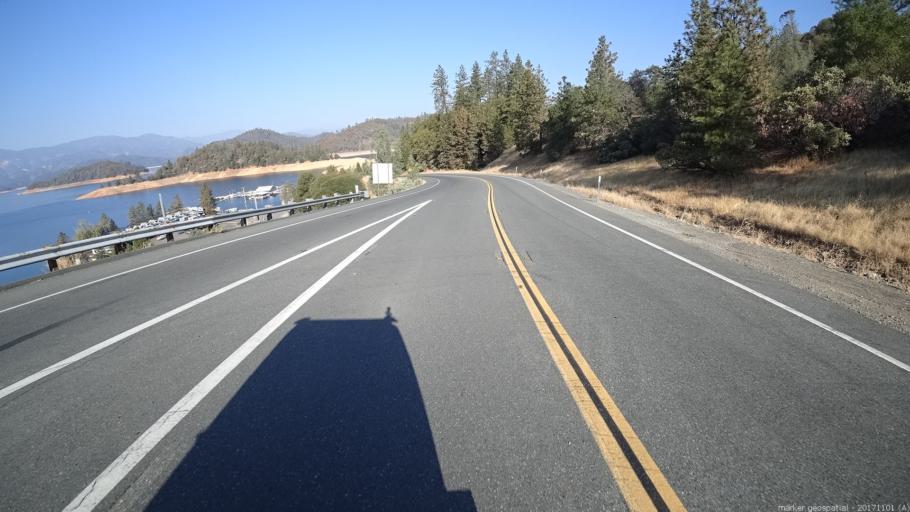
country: US
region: California
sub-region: Shasta County
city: Shasta Lake
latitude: 40.7519
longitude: -122.3216
